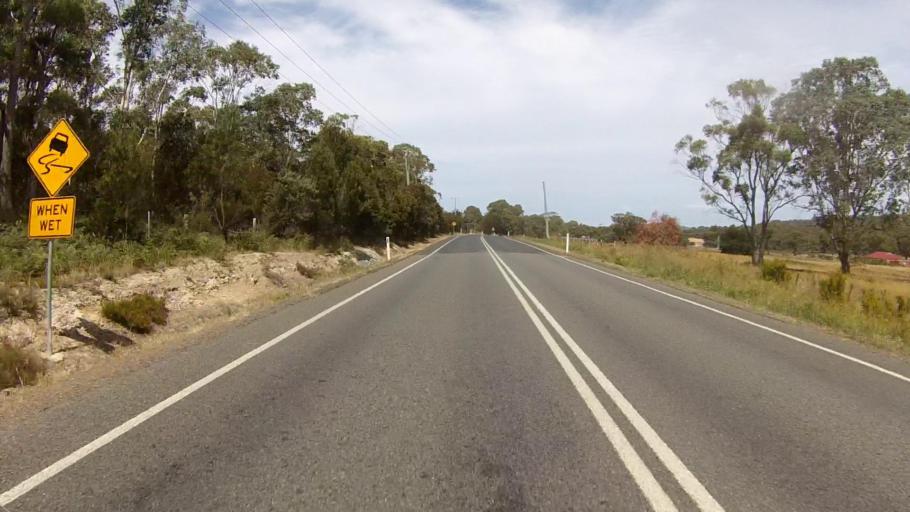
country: AU
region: Tasmania
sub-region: Clarence
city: Sandford
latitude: -42.9951
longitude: 147.5001
